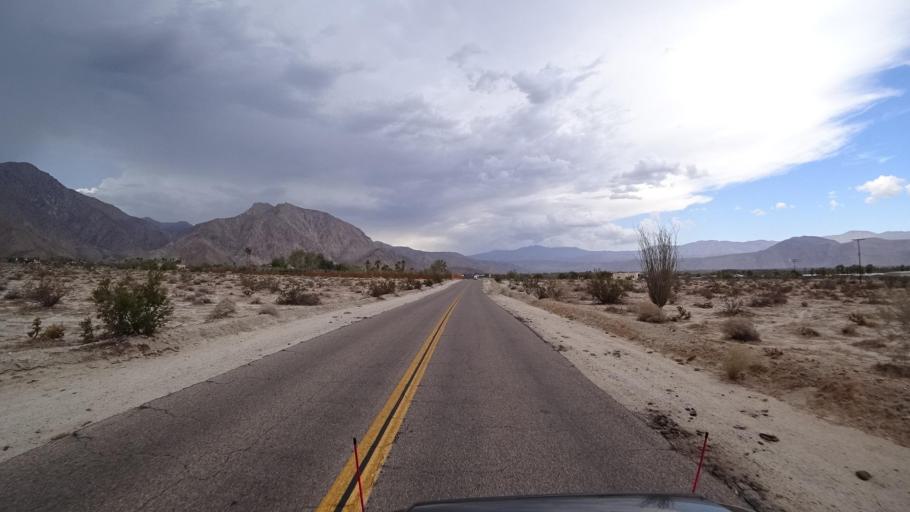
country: US
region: California
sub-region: San Diego County
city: Borrego Springs
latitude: 33.2603
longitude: -116.3868
